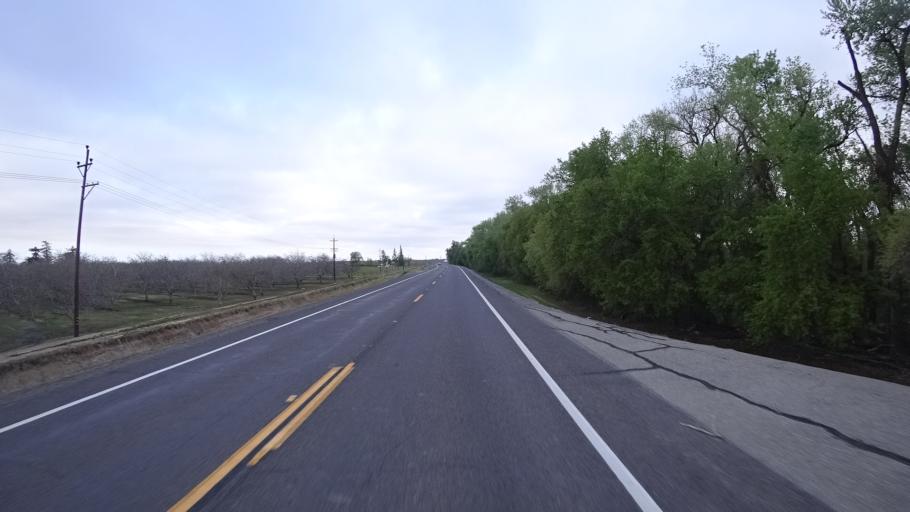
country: US
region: California
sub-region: Glenn County
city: Willows
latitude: 39.4452
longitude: -122.0154
